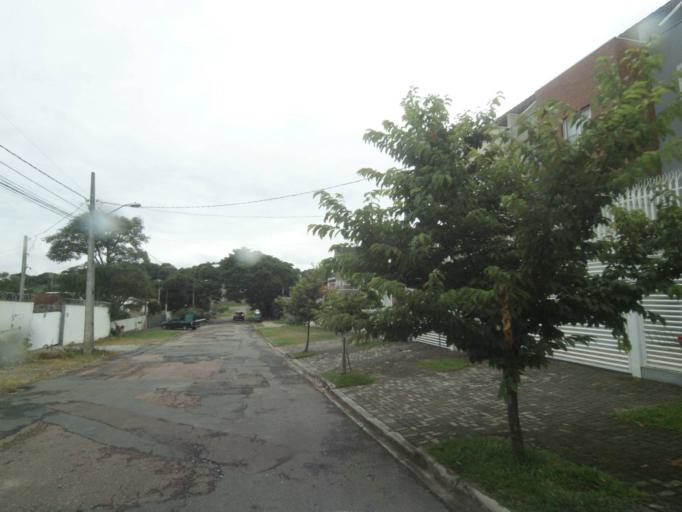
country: BR
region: Parana
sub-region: Curitiba
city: Curitiba
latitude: -25.4280
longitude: -49.3204
